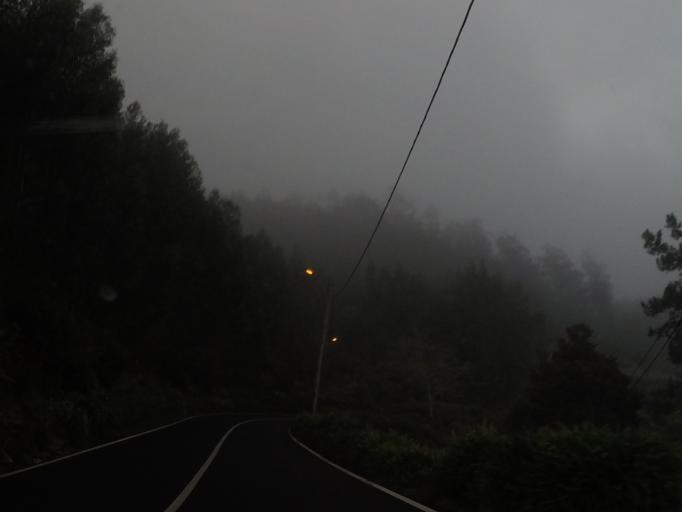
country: PT
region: Madeira
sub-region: Santa Cruz
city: Camacha
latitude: 32.7092
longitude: -16.8324
